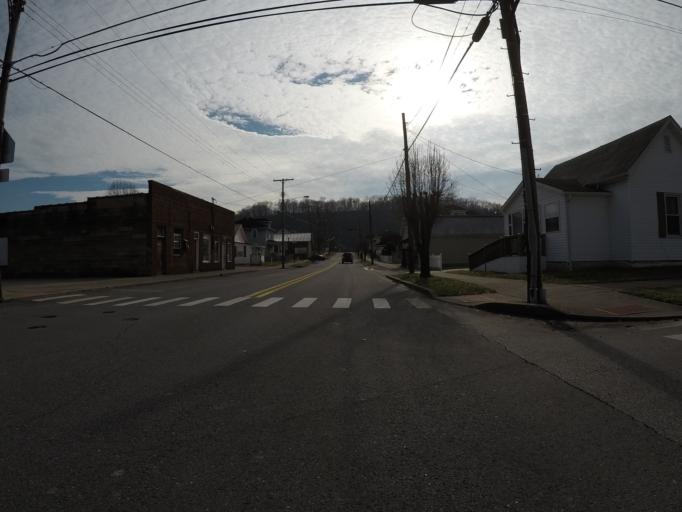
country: US
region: West Virginia
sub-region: Cabell County
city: Barboursville
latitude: 38.4056
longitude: -82.2952
